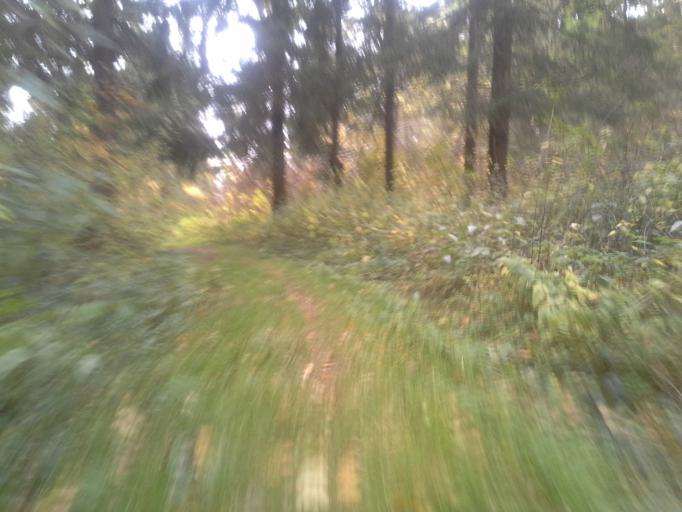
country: RU
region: Moskovskaya
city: Selyatino
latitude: 55.4642
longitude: 36.9530
